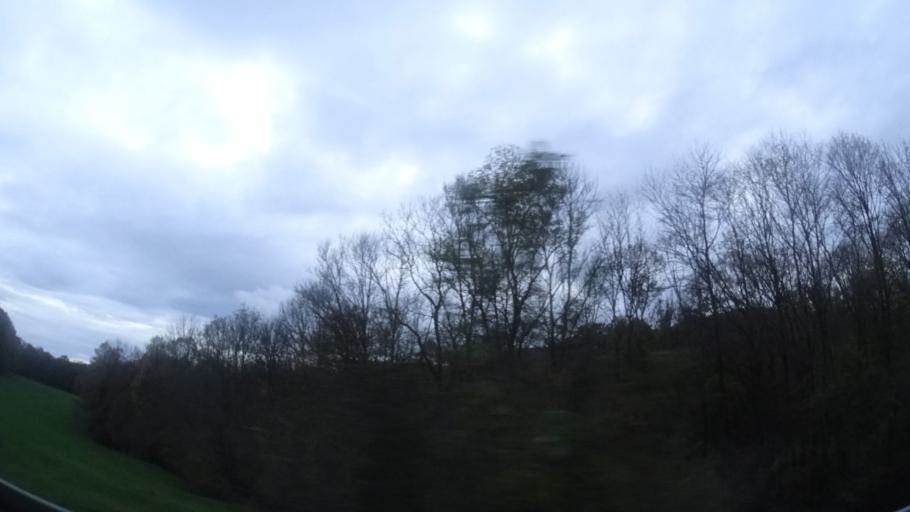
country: DE
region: Hesse
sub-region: Regierungsbezirk Darmstadt
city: Steinau an der Strasse
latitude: 50.3346
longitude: 9.4299
